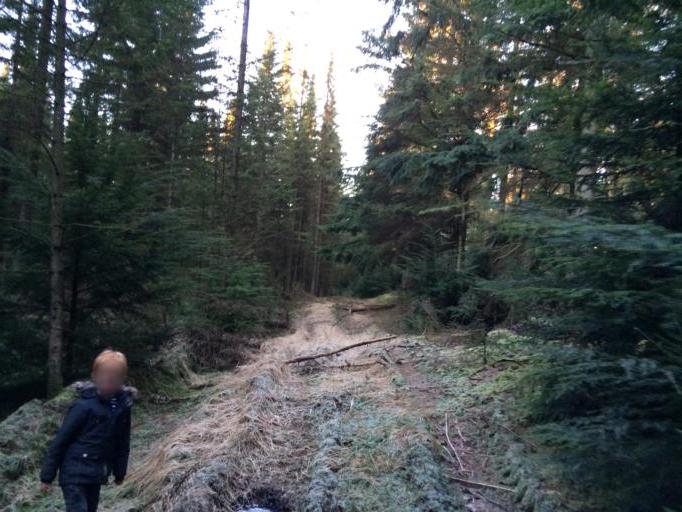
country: DK
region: Central Jutland
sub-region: Holstebro Kommune
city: Ulfborg
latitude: 56.2522
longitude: 8.4484
